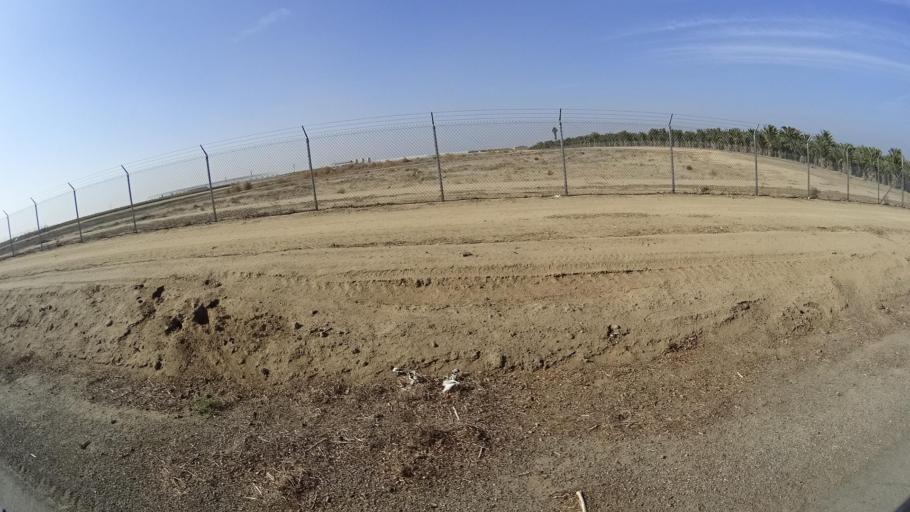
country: US
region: California
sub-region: Kern County
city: McFarland
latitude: 35.6143
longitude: -119.1333
